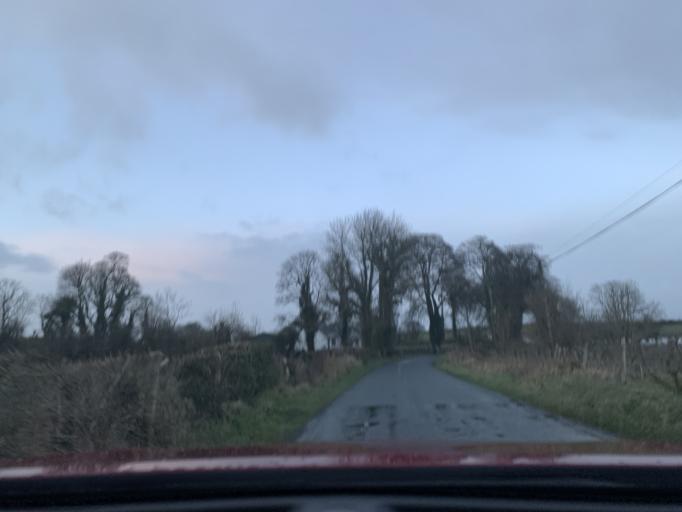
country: IE
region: Connaught
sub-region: Sligo
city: Ballymote
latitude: 54.0436
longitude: -8.6092
